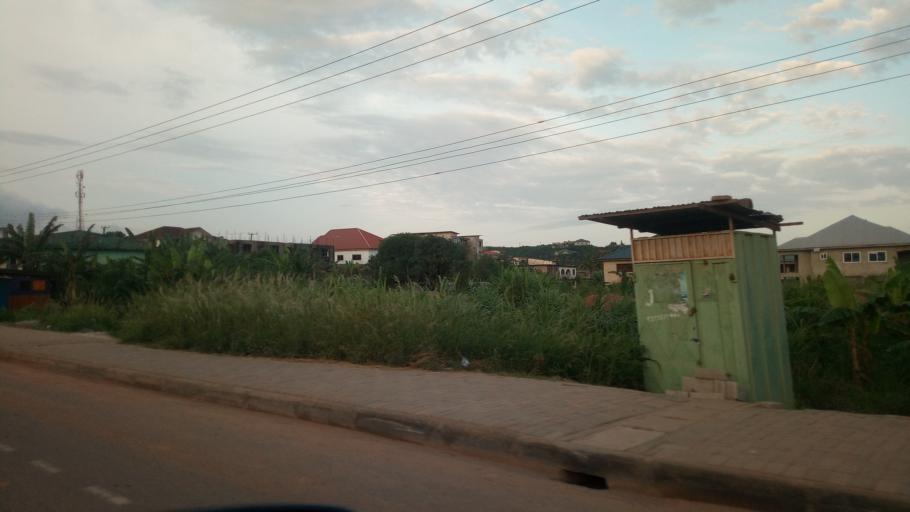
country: GH
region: Western
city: Sekondi-Takoradi
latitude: 4.9465
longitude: -1.7641
